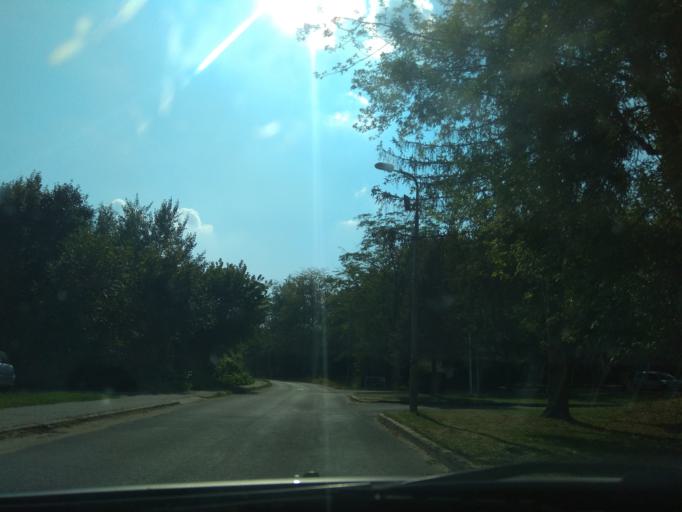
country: HU
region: Borsod-Abauj-Zemplen
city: Miskolc
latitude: 48.0780
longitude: 20.7628
